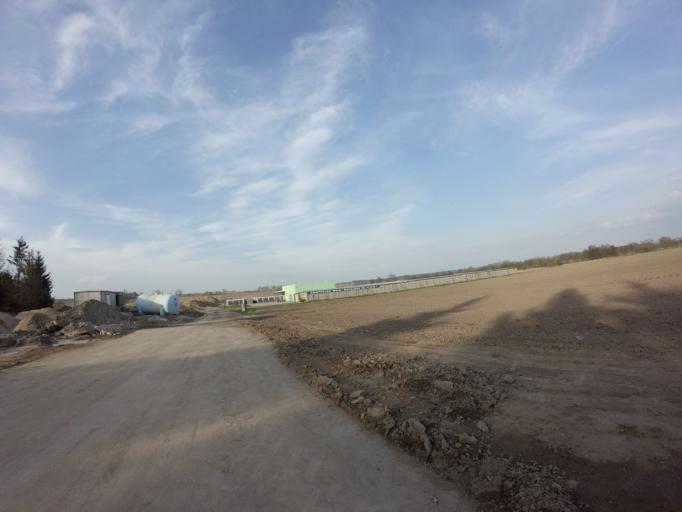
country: PL
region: West Pomeranian Voivodeship
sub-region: Powiat choszczenski
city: Choszczno
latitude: 53.1718
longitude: 15.4471
